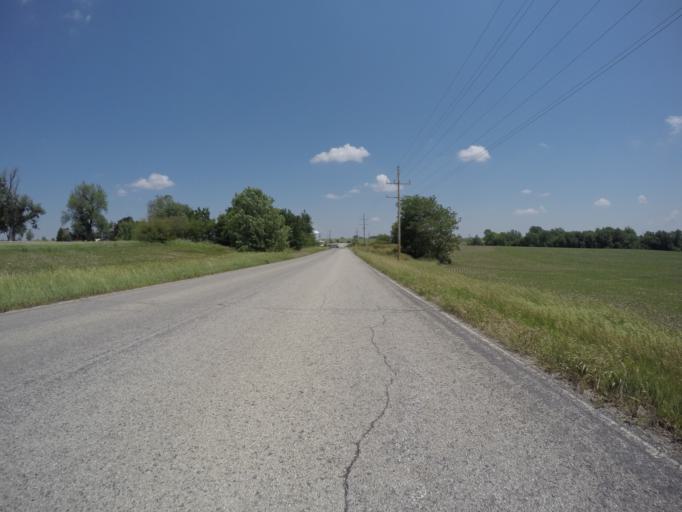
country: US
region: Kansas
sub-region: Doniphan County
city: Troy
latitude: 39.7684
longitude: -95.1189
